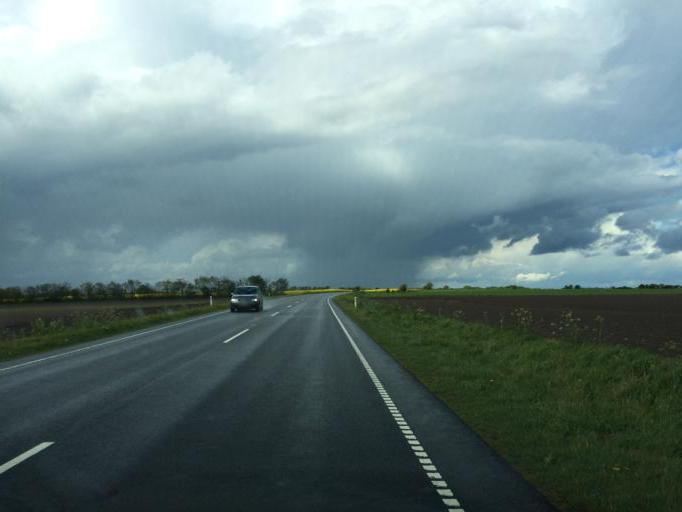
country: DK
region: North Denmark
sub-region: Vesthimmerland Kommune
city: Farso
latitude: 56.6785
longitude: 9.3436
